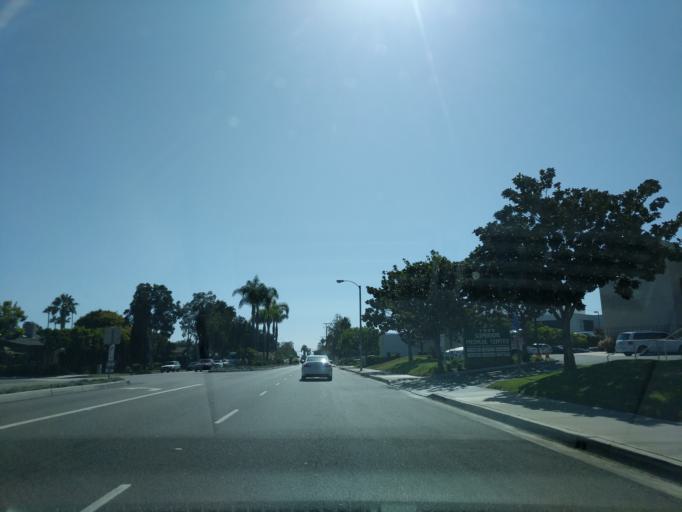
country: US
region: California
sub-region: Orange County
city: Newport Beach
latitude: 33.6299
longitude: -117.9299
